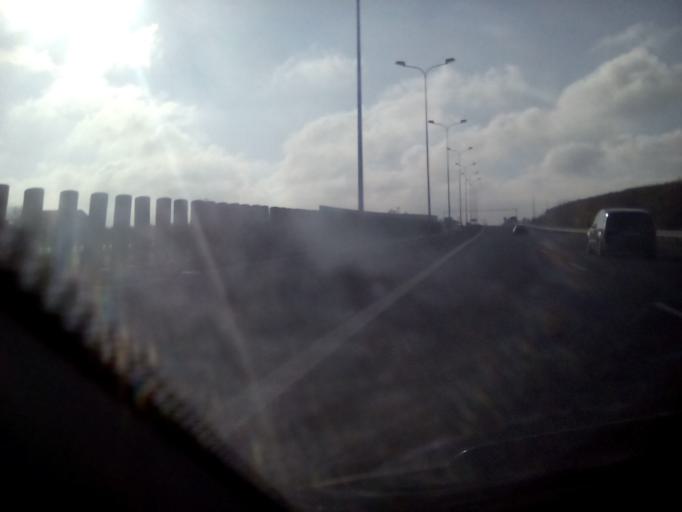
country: PL
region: Masovian Voivodeship
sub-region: Powiat grojecki
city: Goszczyn
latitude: 51.7578
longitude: 20.9052
